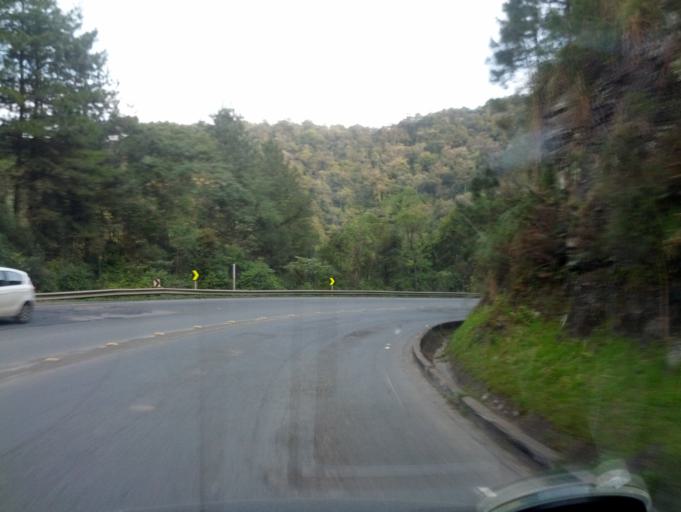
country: BR
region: Santa Catarina
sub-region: Otacilio Costa
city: Otacilio Costa
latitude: -27.3006
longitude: -50.0797
